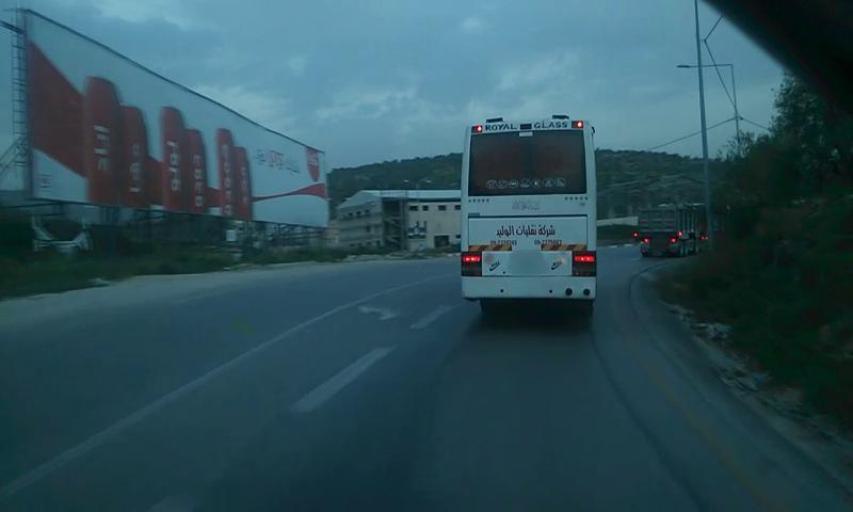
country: PS
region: West Bank
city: Kafr al Labad
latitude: 32.3168
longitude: 35.0918
